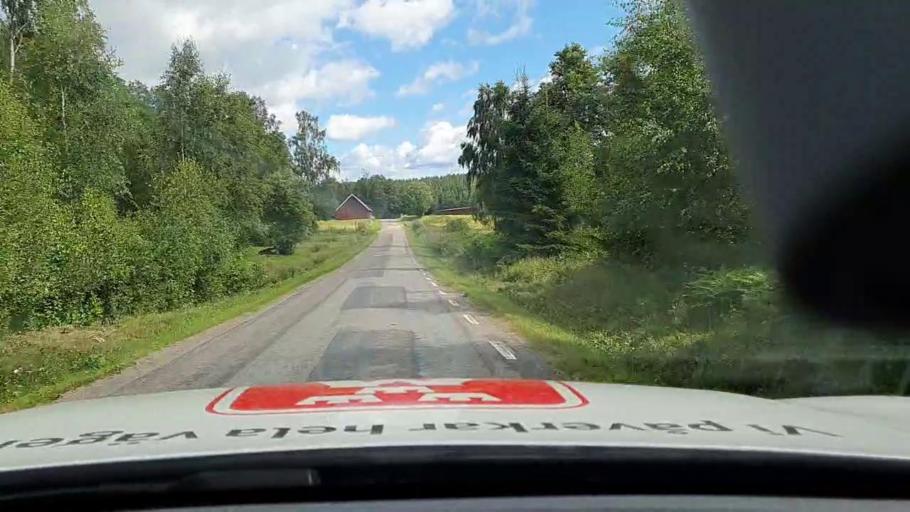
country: SE
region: Vaestra Goetaland
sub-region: Karlsborgs Kommun
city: Molltorp
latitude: 58.6040
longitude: 14.3052
